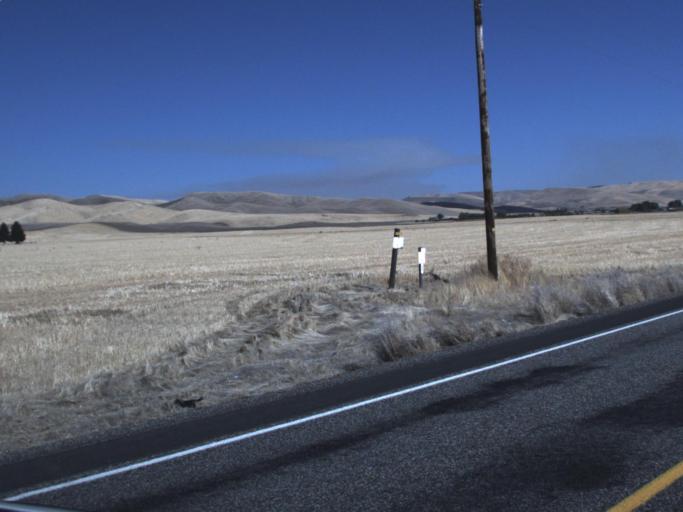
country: US
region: Washington
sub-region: Walla Walla County
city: Waitsburg
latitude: 46.2988
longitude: -118.3361
